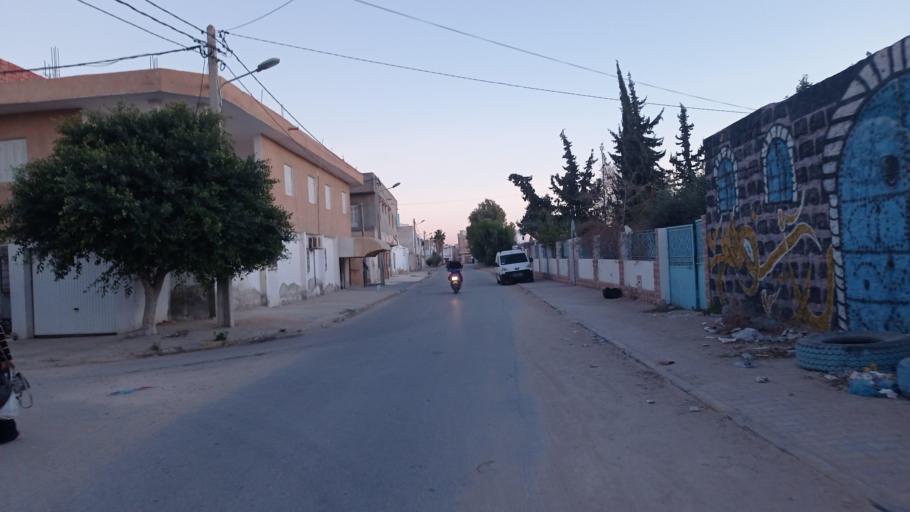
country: TN
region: Qabis
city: Gabes
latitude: 33.8457
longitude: 10.1154
